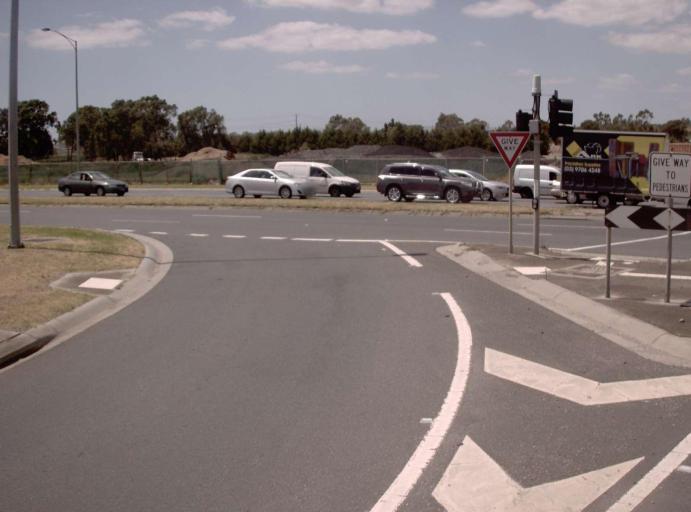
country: AU
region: Victoria
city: Heatherton
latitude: -37.9663
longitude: 145.1106
